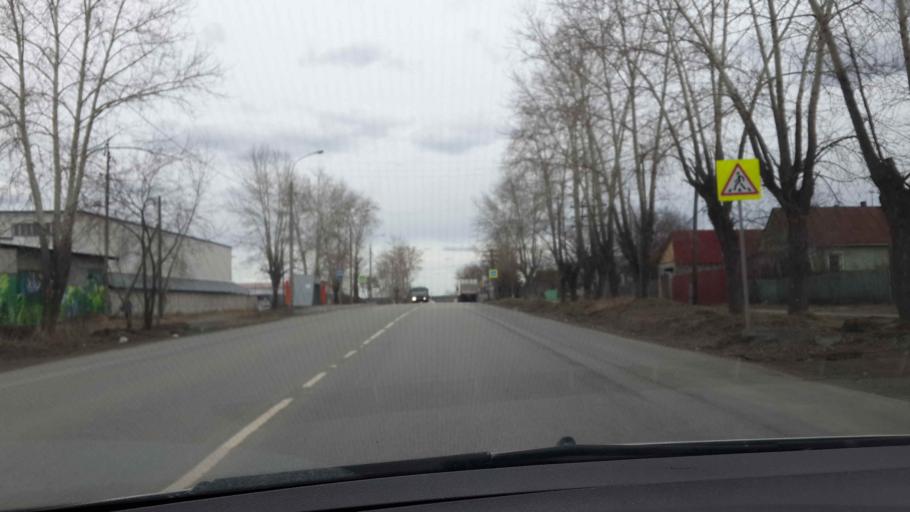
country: RU
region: Sverdlovsk
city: Beloyarskiy
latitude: 56.7566
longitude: 61.3560
